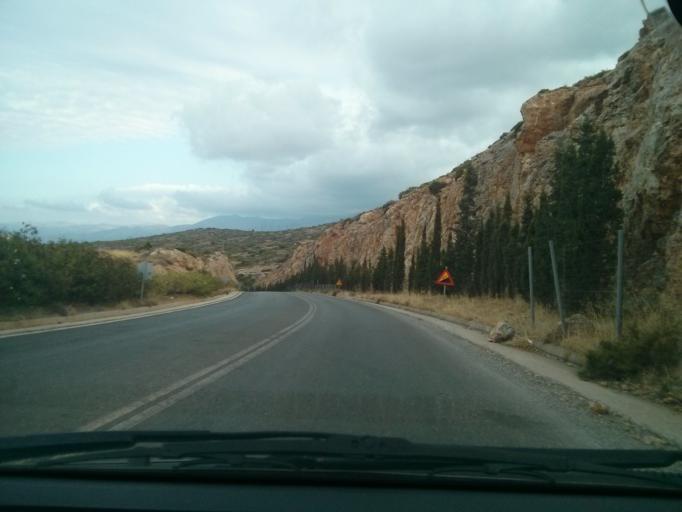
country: GR
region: Crete
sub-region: Nomos Irakleiou
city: Limin Khersonisou
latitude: 35.2994
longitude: 25.4013
